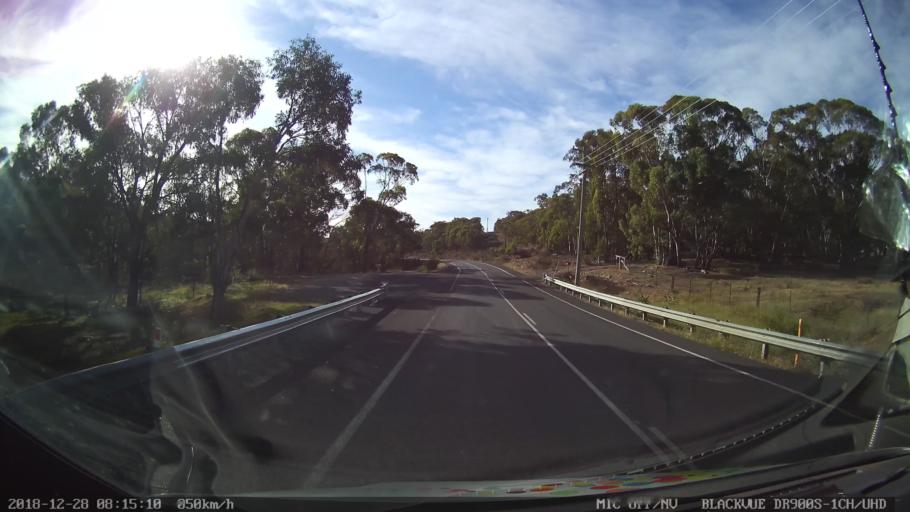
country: AU
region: New South Wales
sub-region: Blayney
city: Blayney
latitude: -33.8218
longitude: 149.3265
